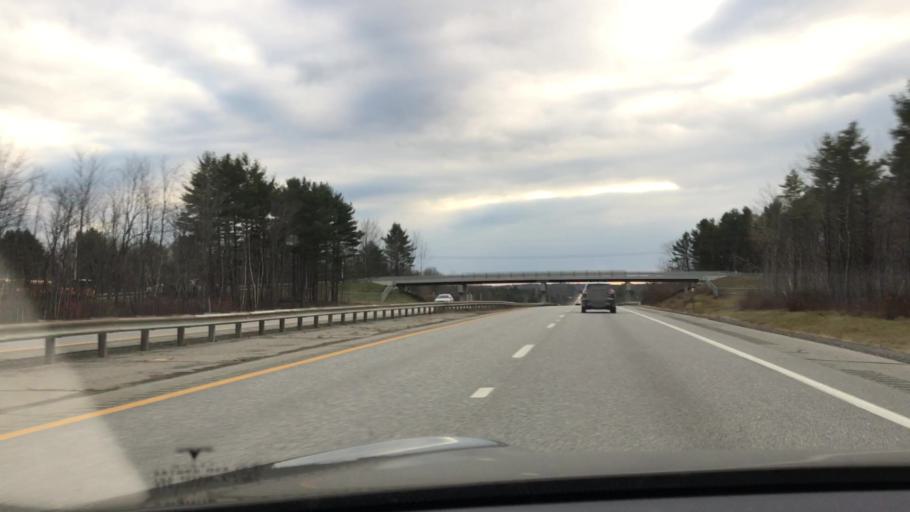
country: US
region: Maine
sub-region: Kennebec County
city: Hallowell
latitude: 44.2655
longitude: -69.8068
